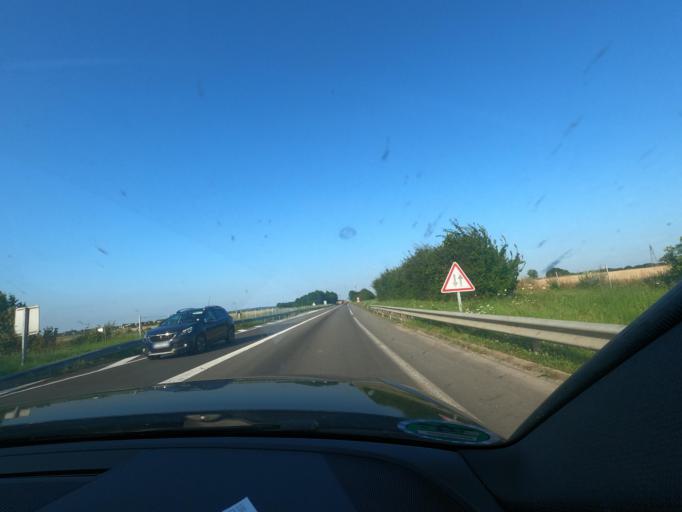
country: FR
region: Picardie
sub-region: Departement de la Somme
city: Pont-de-Metz
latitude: 49.8944
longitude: 2.2448
